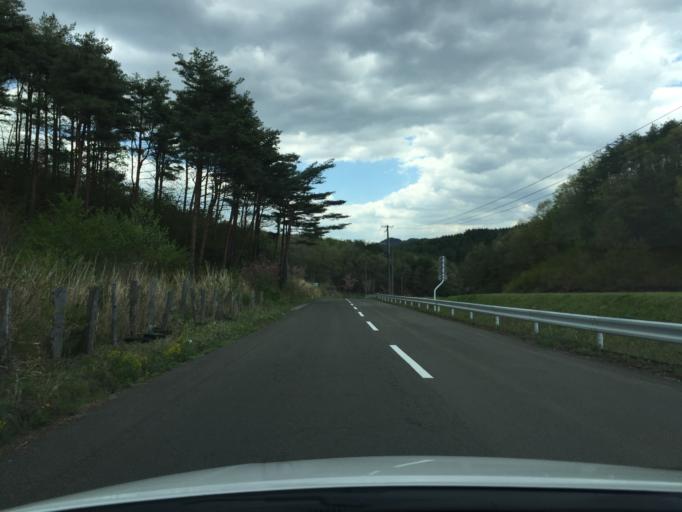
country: JP
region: Fukushima
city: Yanagawamachi-saiwaicho
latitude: 37.7295
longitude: 140.6778
